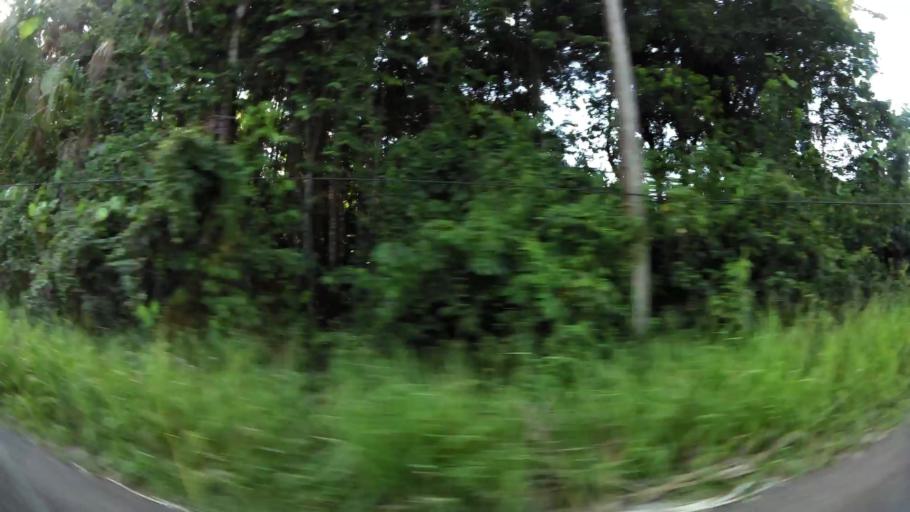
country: GF
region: Guyane
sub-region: Guyane
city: Remire-Montjoly
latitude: 4.8885
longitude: -52.2938
